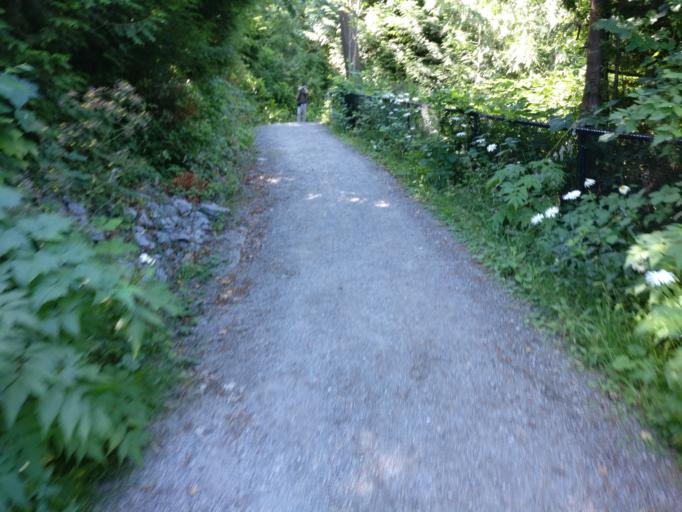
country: CA
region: British Columbia
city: West End
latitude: 49.3102
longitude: -123.1521
